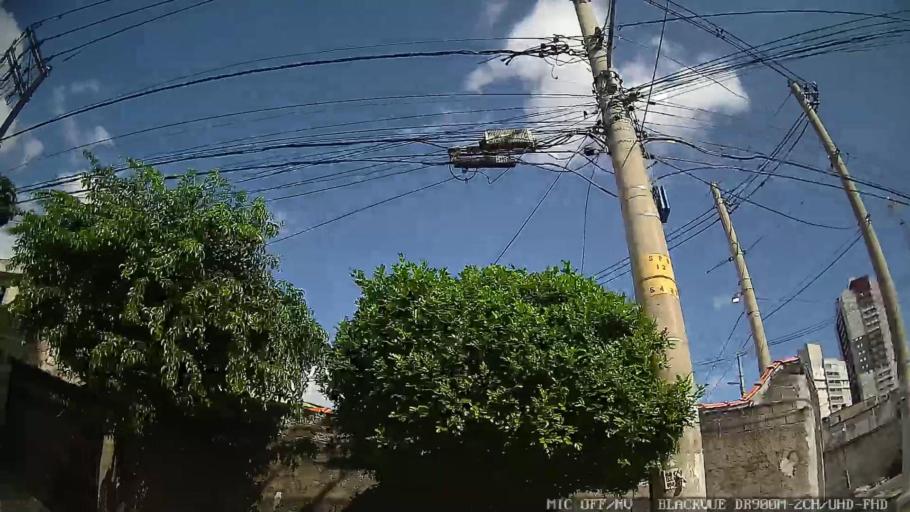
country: BR
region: Sao Paulo
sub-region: Guarulhos
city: Guarulhos
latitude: -23.4868
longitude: -46.4846
